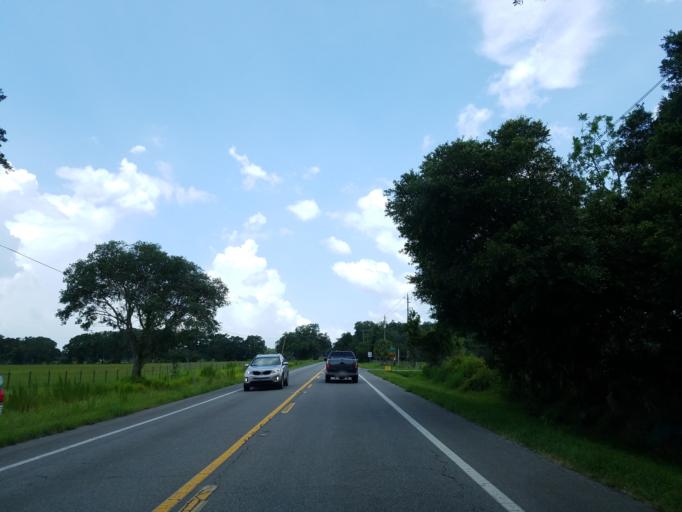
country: US
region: Florida
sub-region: Hillsborough County
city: Fish Hawk
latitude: 27.8506
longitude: -82.1261
